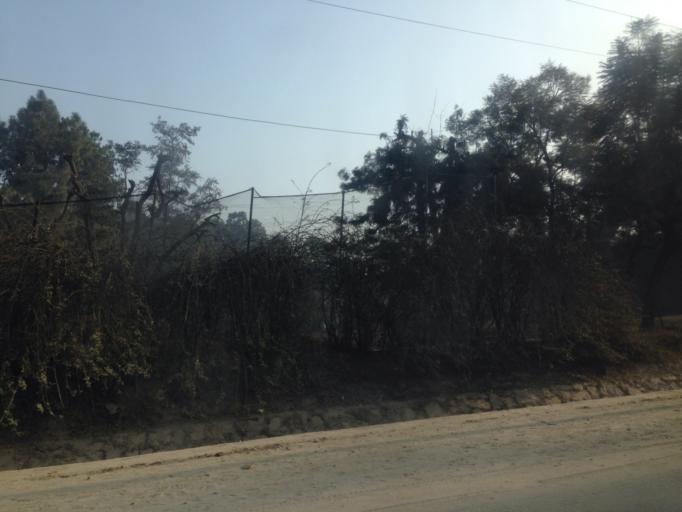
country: NP
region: Central Region
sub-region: Bagmati Zone
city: Kathmandu
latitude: 27.7061
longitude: 85.3512
